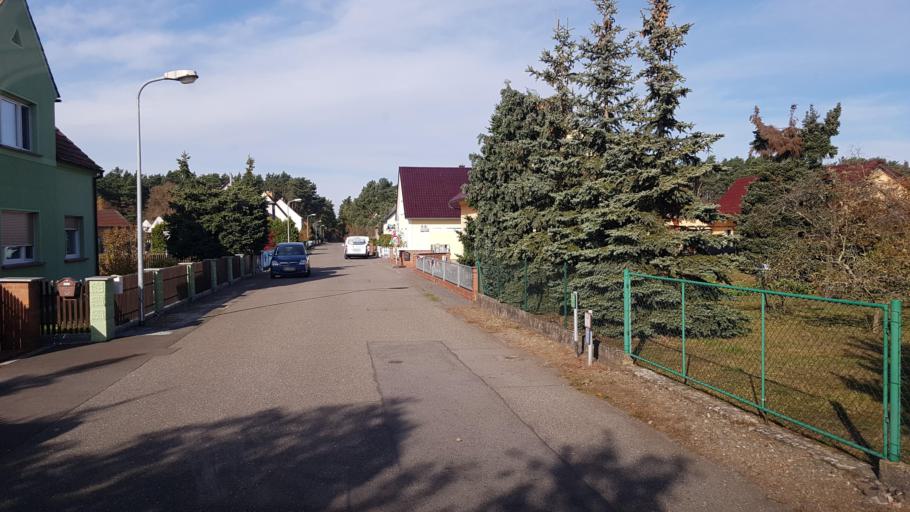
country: DE
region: Brandenburg
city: Tettau
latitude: 51.4205
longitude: 13.7667
